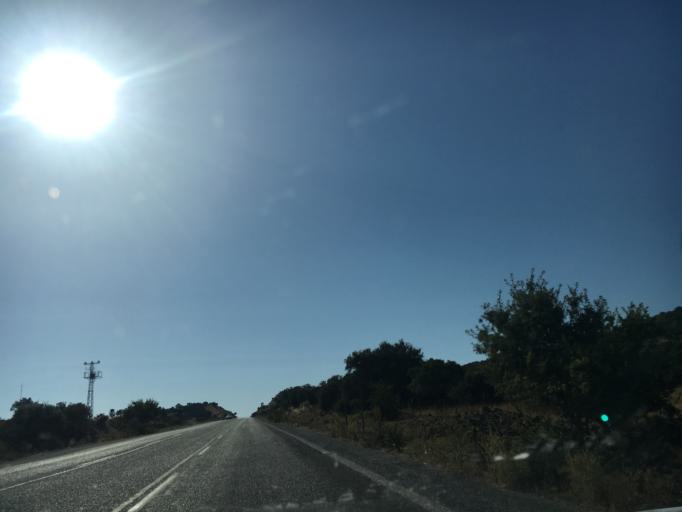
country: TR
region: Canakkale
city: Behram
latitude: 39.5053
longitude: 26.3976
